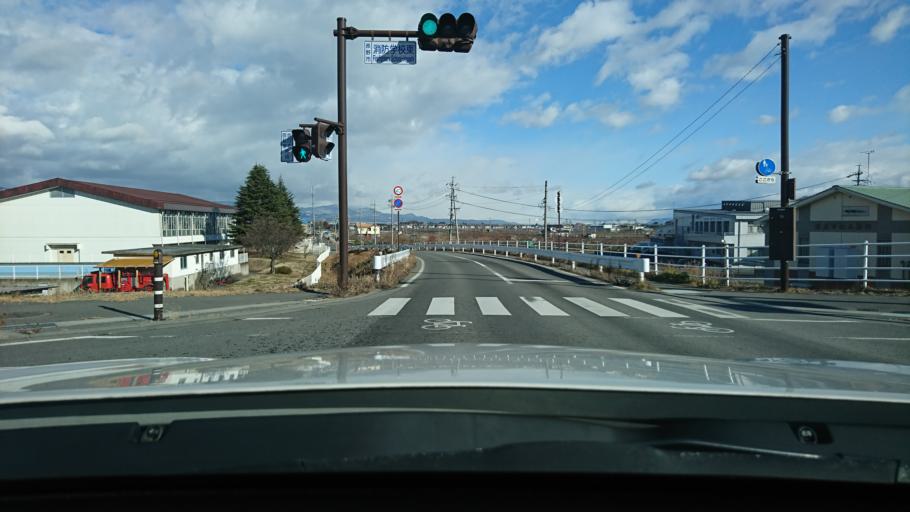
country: JP
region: Nagano
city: Nagano-shi
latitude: 36.5700
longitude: 138.1753
